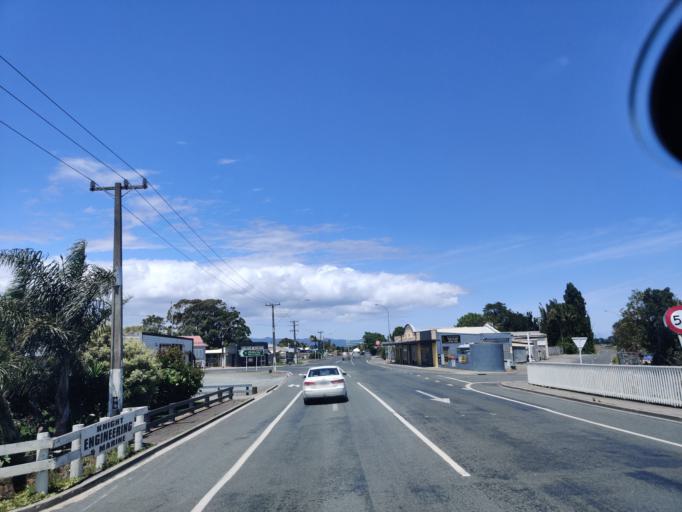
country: NZ
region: Northland
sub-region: Far North District
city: Kaitaia
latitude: -35.0456
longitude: 173.2566
